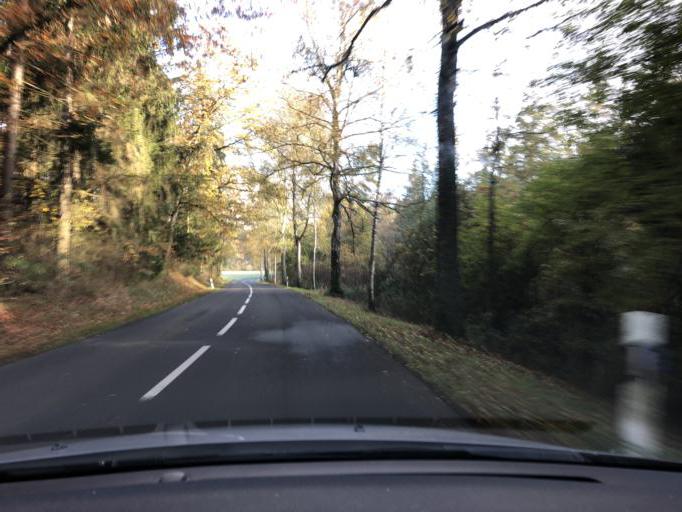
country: DE
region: Thuringia
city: Reurieth
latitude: 50.4288
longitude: 10.6322
